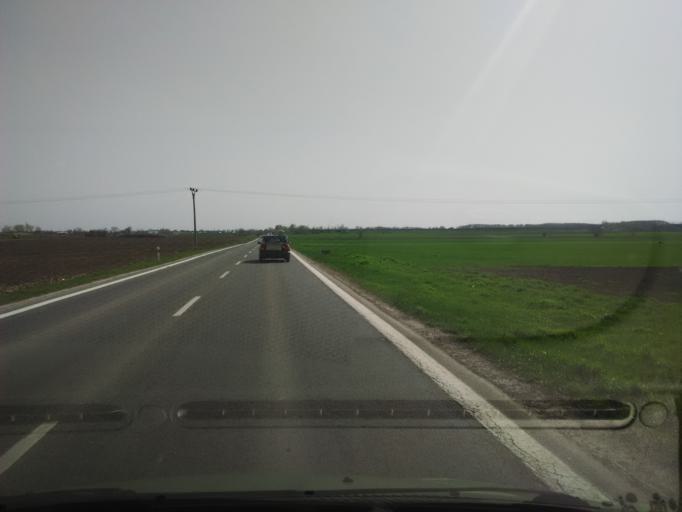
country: SK
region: Nitriansky
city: Sellye
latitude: 48.1646
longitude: 17.9015
